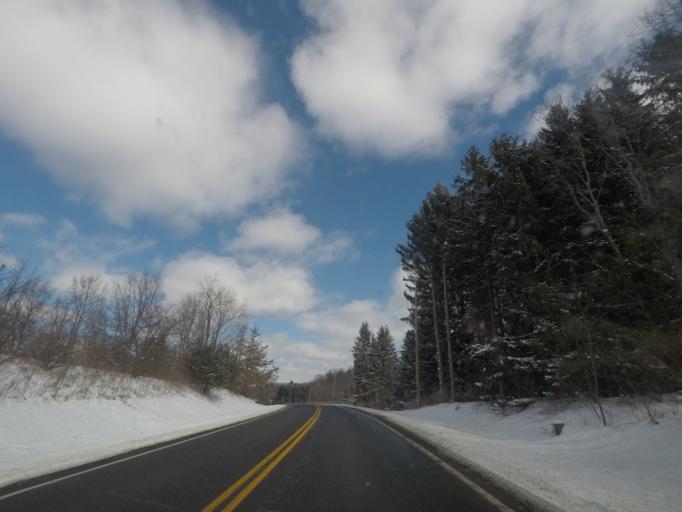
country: US
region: New York
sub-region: Rensselaer County
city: Nassau
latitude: 42.4610
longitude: -73.5422
